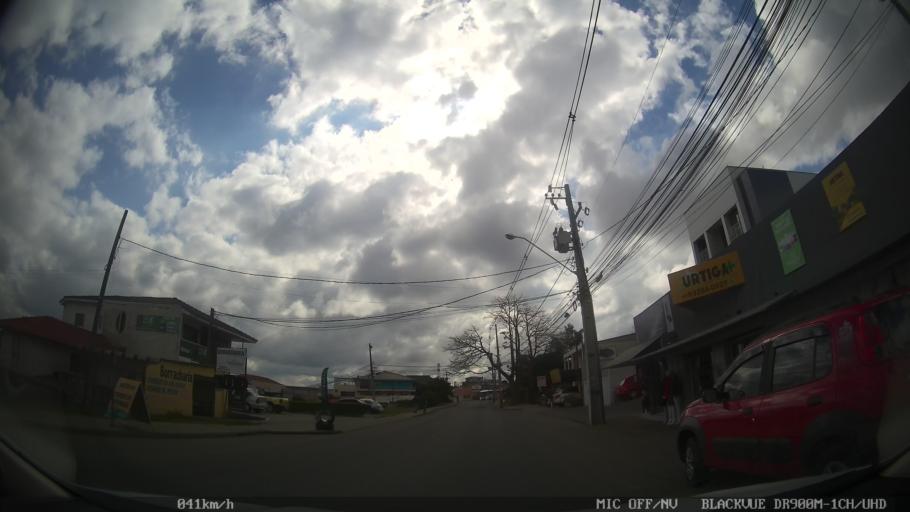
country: BR
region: Parana
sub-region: Pinhais
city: Pinhais
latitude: -25.3701
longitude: -49.2006
